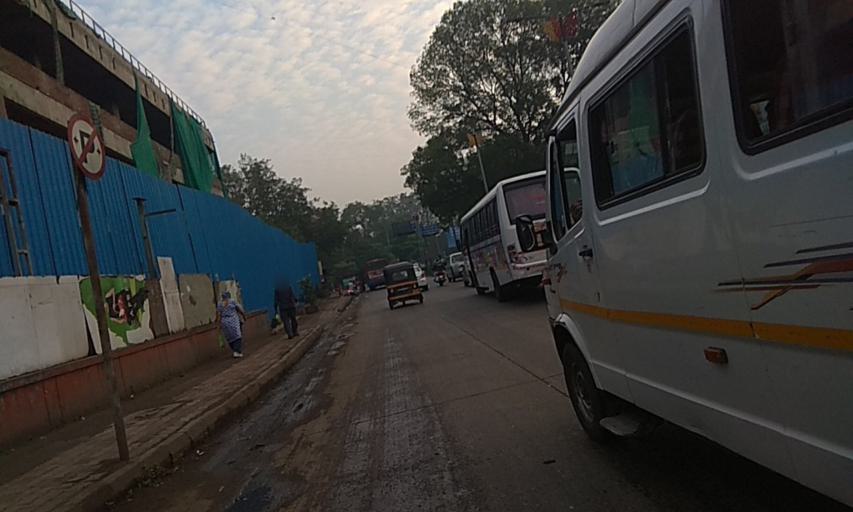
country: IN
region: Maharashtra
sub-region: Pune Division
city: Shivaji Nagar
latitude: 18.5402
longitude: 73.8829
